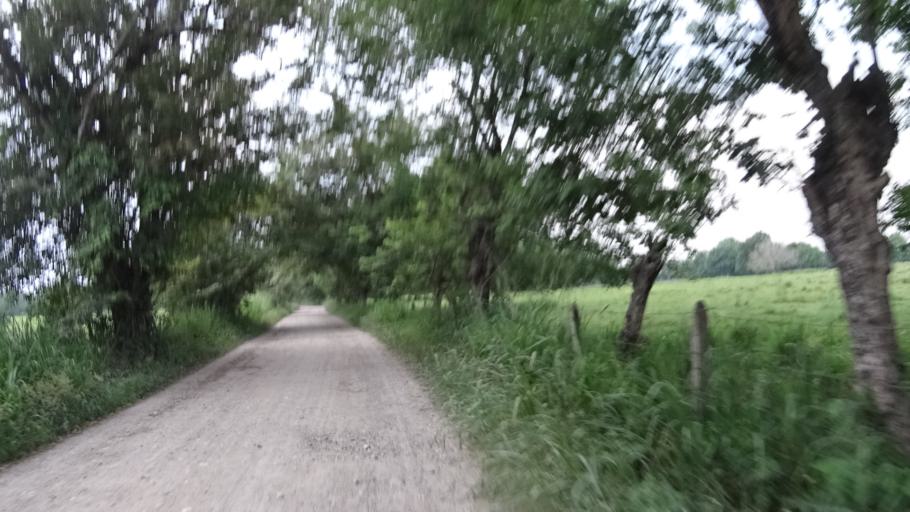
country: CO
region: Cundinamarca
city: Puerto Salgar
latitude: 5.4846
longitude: -74.6891
